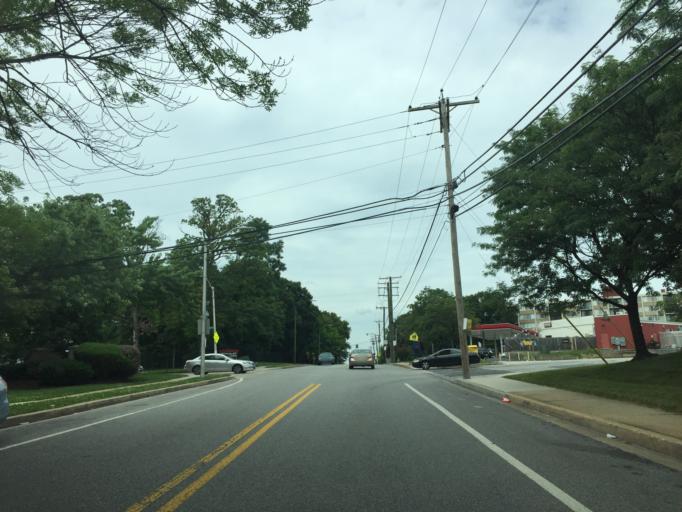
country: US
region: Maryland
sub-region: Baltimore County
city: Parkville
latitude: 39.3668
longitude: -76.5670
